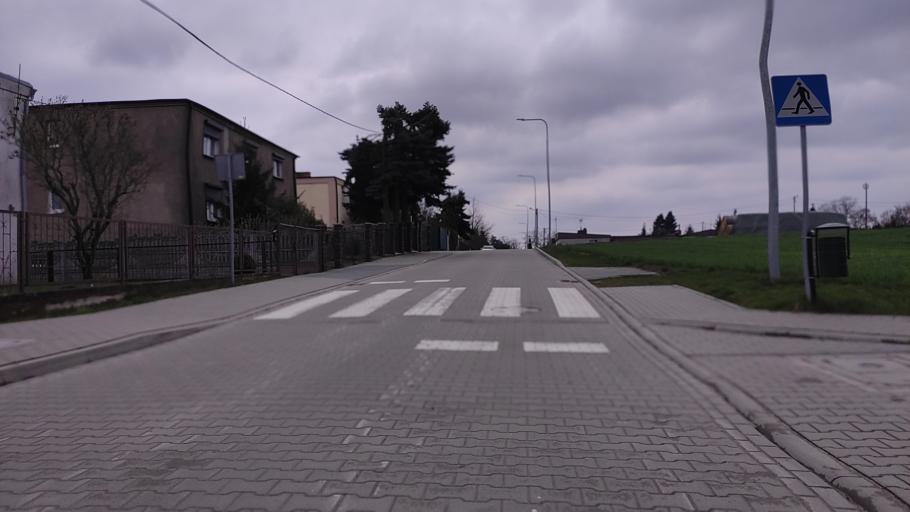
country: PL
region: Greater Poland Voivodeship
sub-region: Powiat poznanski
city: Kostrzyn
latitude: 52.4003
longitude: 17.1627
